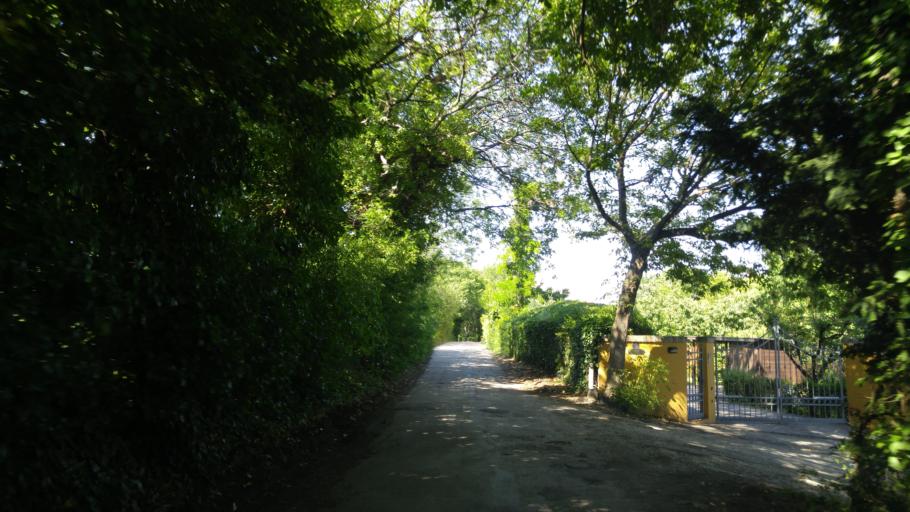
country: IT
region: The Marches
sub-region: Provincia di Pesaro e Urbino
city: Centinarola
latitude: 43.8449
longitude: 12.9899
